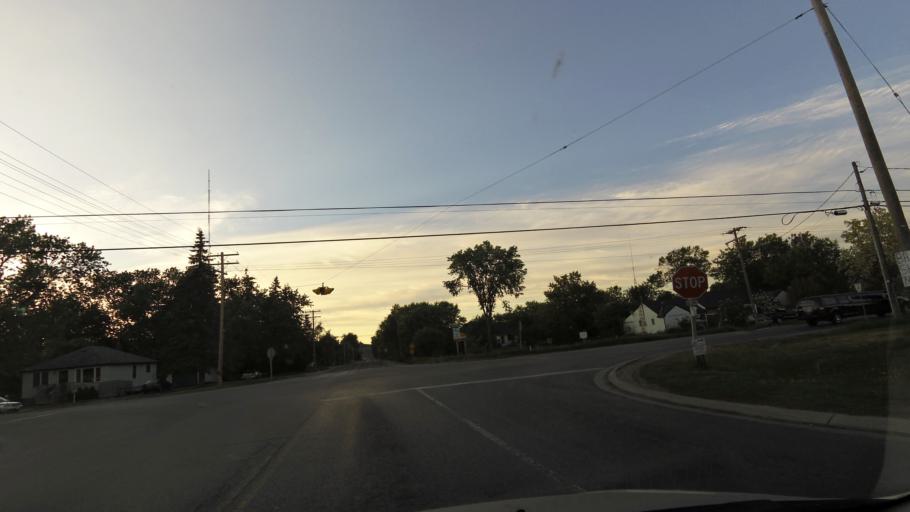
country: CA
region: Ontario
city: Peterborough
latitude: 44.3221
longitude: -78.2931
